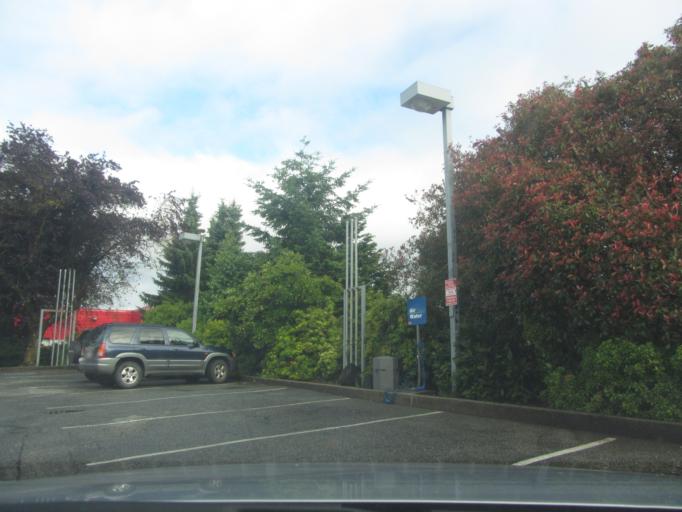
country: CA
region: British Columbia
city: Abbotsford
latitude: 49.0514
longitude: -122.3103
